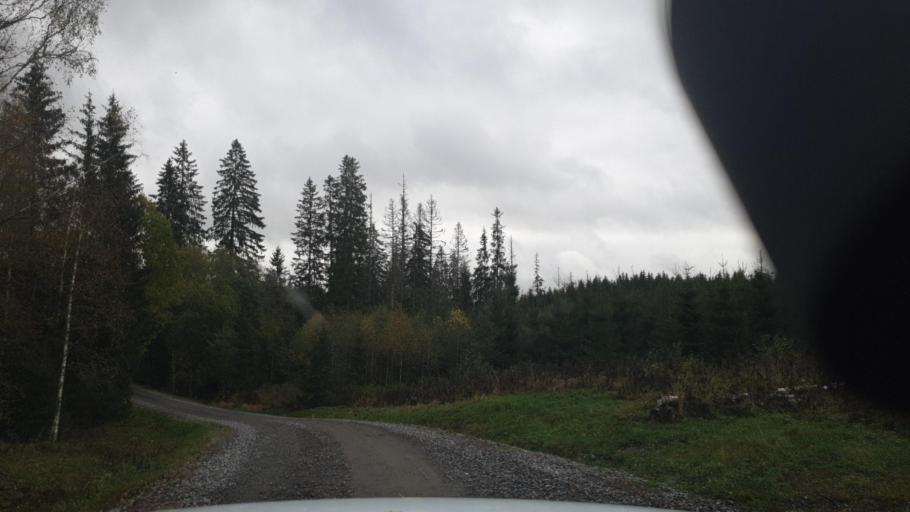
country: SE
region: Vaermland
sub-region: Karlstads Kommun
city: Edsvalla
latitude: 59.4615
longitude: 13.1093
